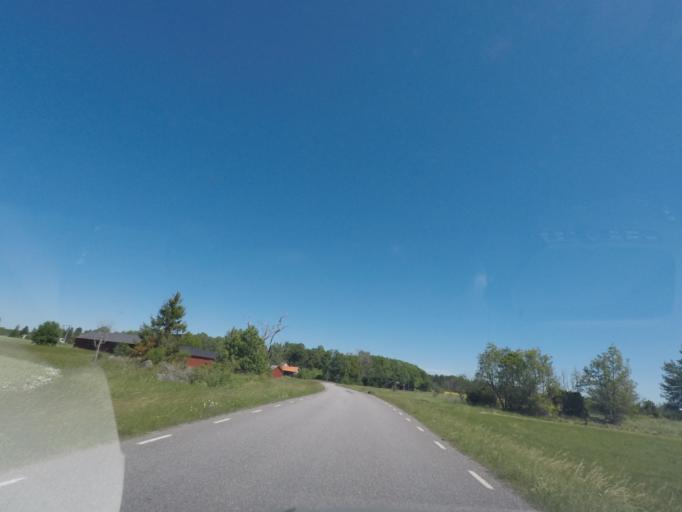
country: SE
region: Uppsala
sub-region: Enkopings Kommun
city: Irsta
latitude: 59.6766
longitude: 16.9175
